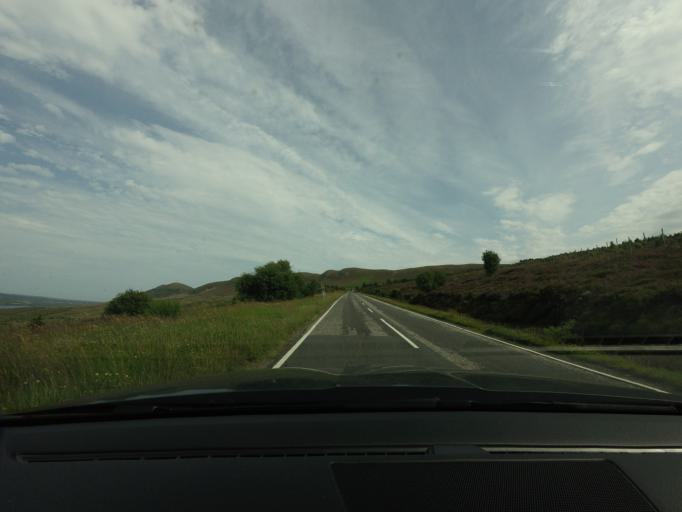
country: GB
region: Scotland
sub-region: Highland
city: Alness
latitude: 57.8425
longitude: -4.2788
